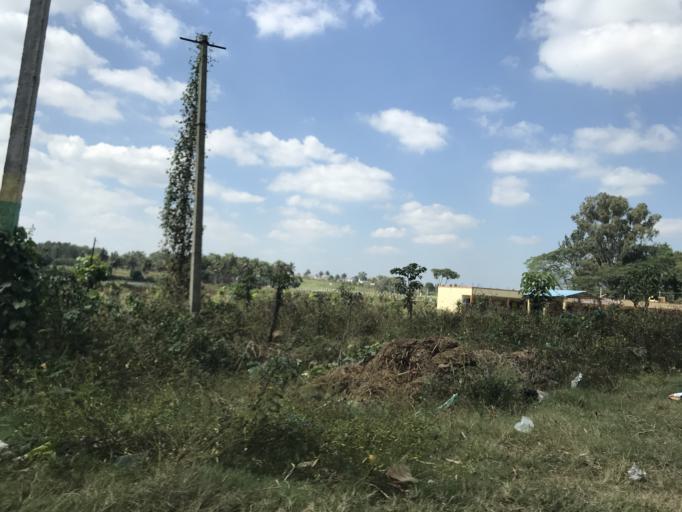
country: IN
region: Karnataka
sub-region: Mysore
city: Hunsur
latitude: 12.2944
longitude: 76.2900
